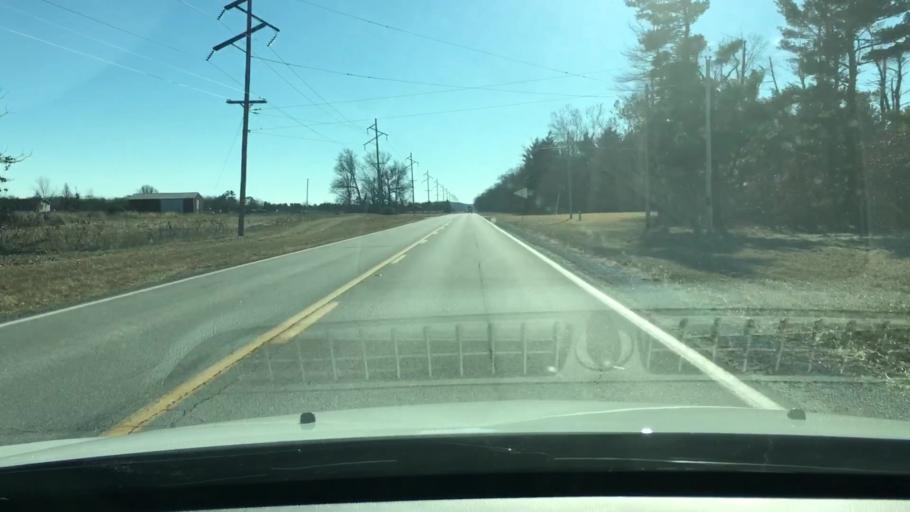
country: US
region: Illinois
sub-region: Morgan County
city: Meredosia
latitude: 39.8861
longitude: -90.5052
